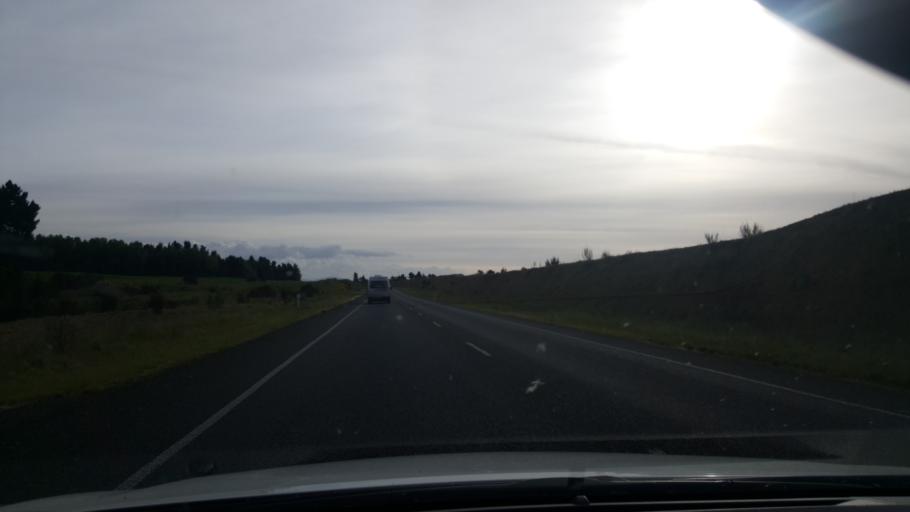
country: NZ
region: Waikato
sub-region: Taupo District
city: Taupo
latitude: -38.7330
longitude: 176.0803
